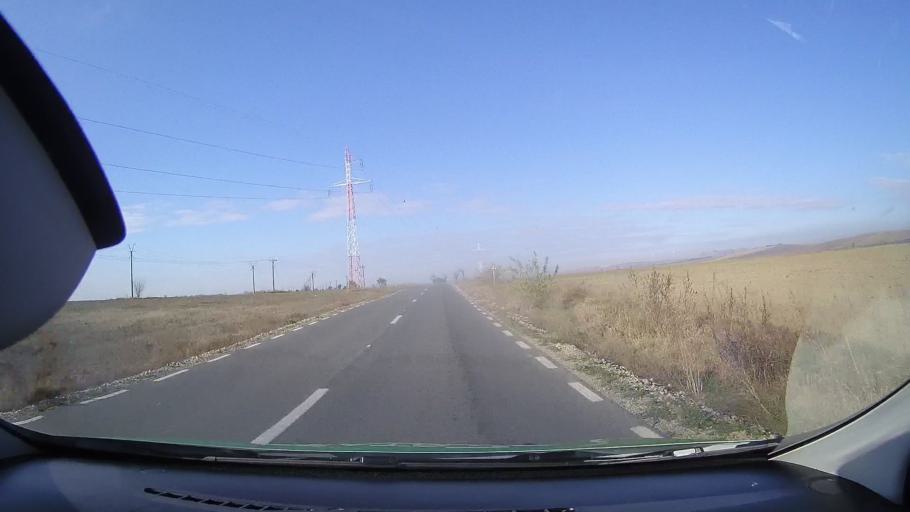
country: RO
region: Tulcea
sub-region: Comuna Murighiol
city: Murighiol
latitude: 45.0283
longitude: 29.1506
